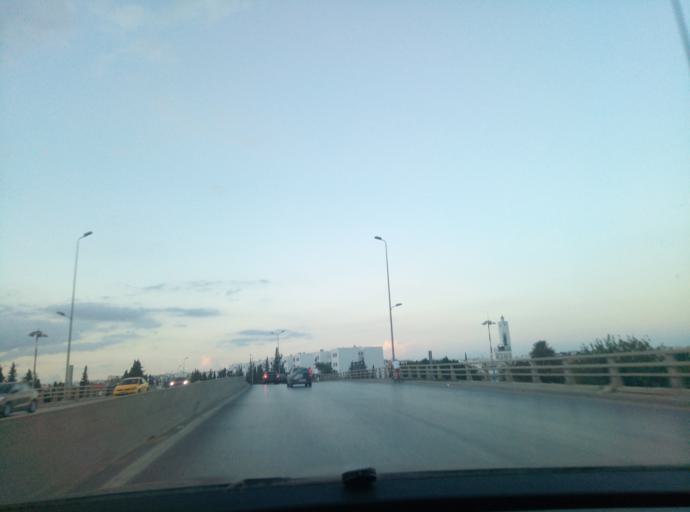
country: TN
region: Manouba
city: Manouba
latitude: 36.8101
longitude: 10.1197
